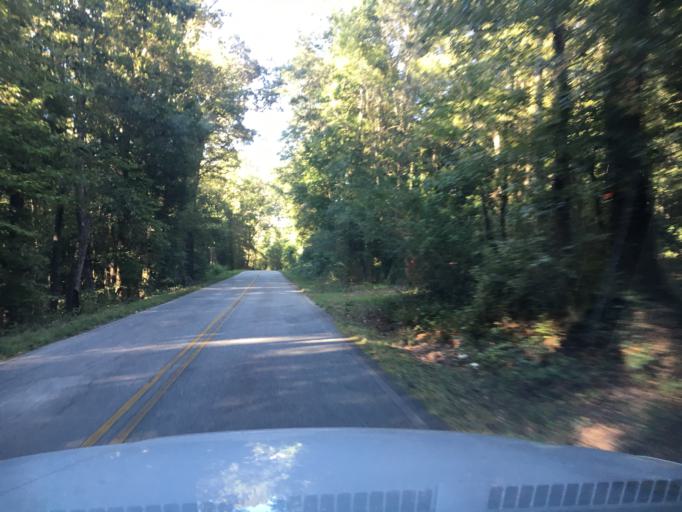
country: US
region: South Carolina
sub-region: Spartanburg County
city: Woodruff
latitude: 34.7923
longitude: -82.1067
